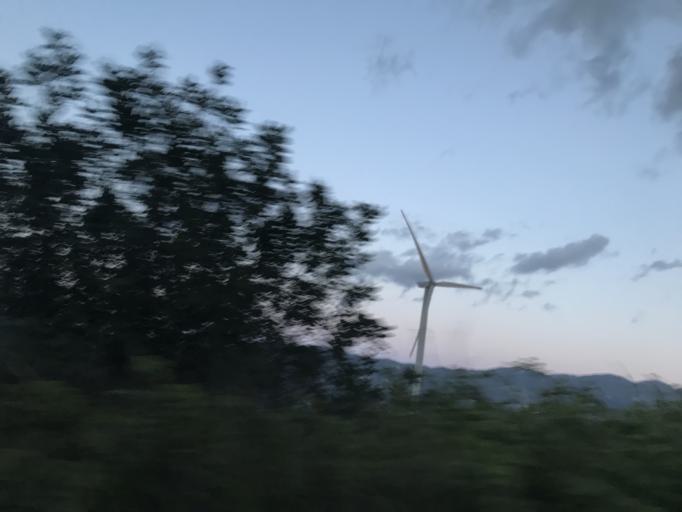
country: TR
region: Hatay
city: Buyukcat
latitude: 36.0985
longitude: 36.0417
